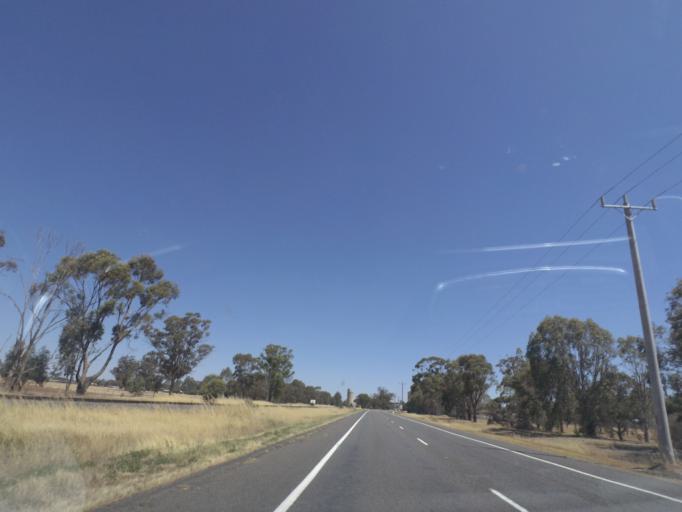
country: AU
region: Victoria
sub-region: Greater Shepparton
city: Shepparton
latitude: -36.2320
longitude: 145.4318
